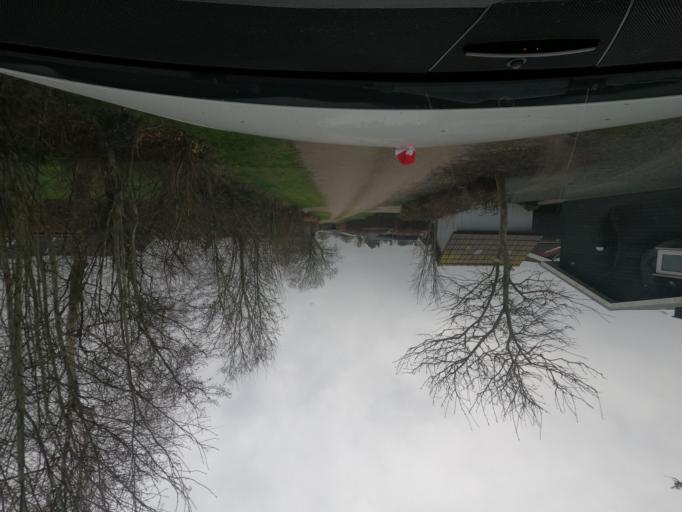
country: DK
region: South Denmark
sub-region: Haderslev Kommune
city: Starup
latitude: 55.2332
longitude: 9.7073
